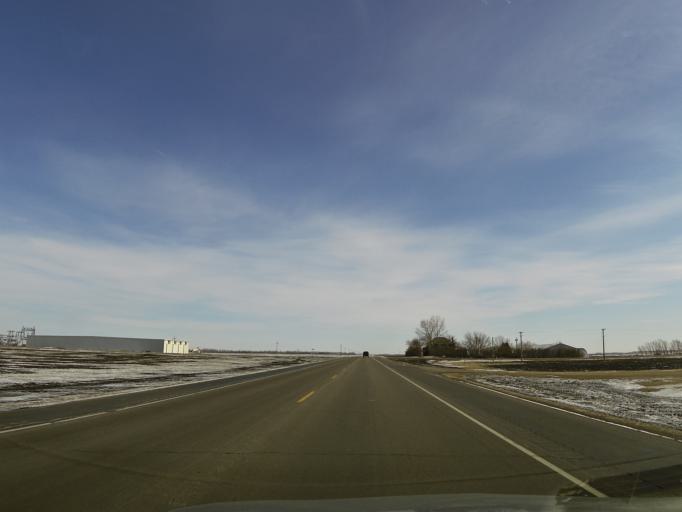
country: US
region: North Dakota
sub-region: Walsh County
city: Grafton
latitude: 48.4126
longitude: -97.3458
